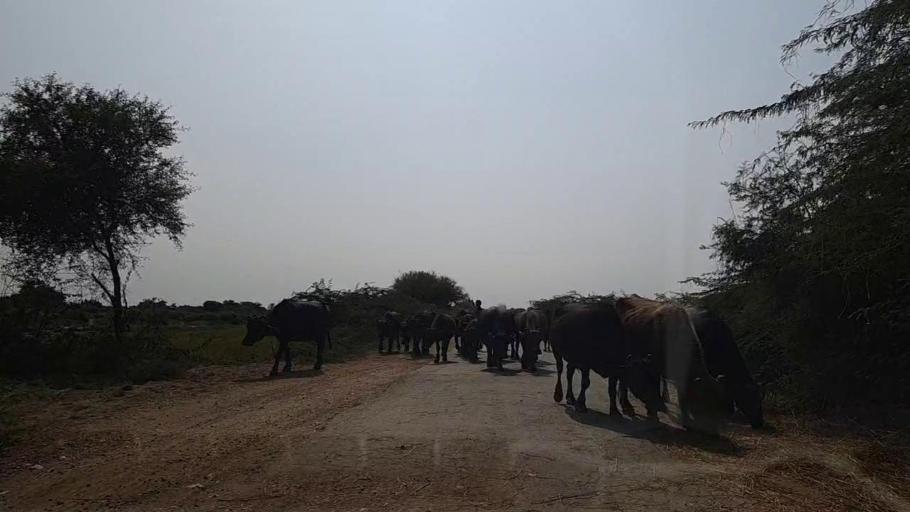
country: PK
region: Sindh
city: Chuhar Jamali
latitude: 24.2543
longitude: 67.9065
